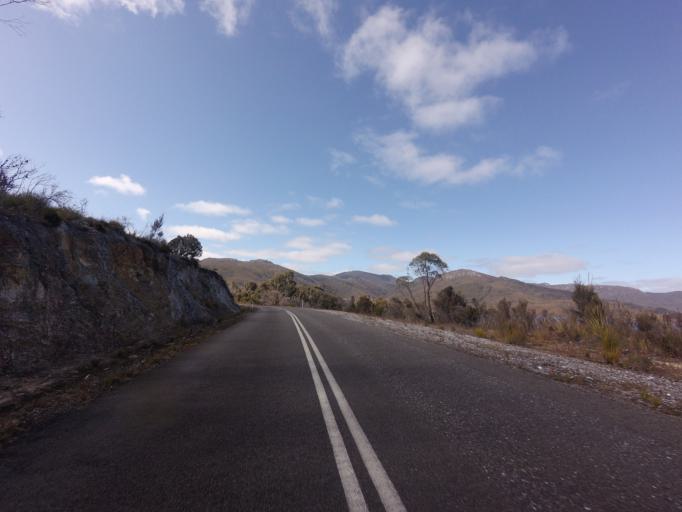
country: AU
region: Tasmania
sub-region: Huon Valley
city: Geeveston
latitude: -42.8432
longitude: 146.1644
